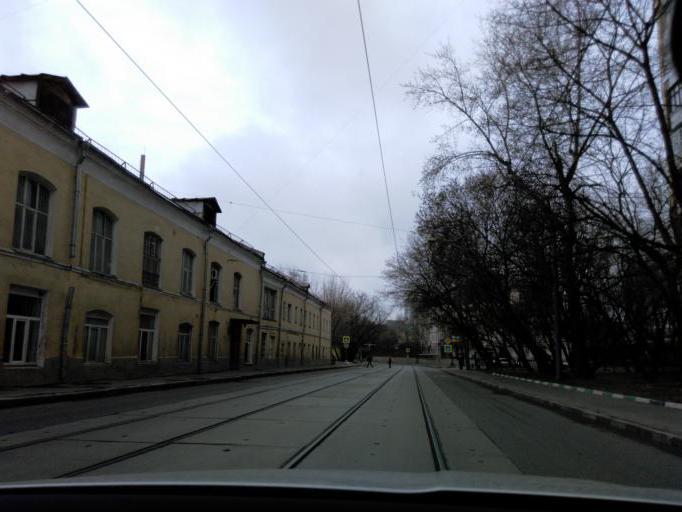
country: RU
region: Moscow
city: Zamoskvorech'ye
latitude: 55.7169
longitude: 37.6336
